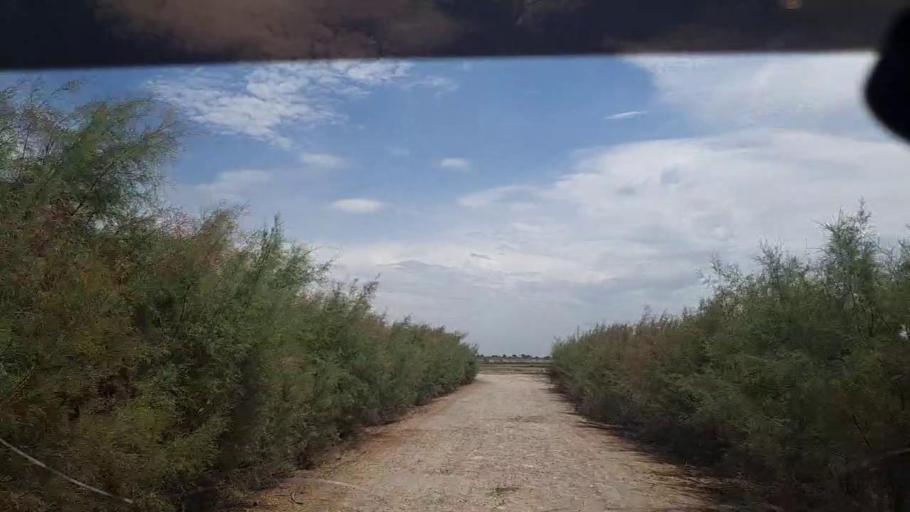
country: PK
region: Sindh
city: Ghauspur
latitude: 28.1442
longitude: 68.9780
